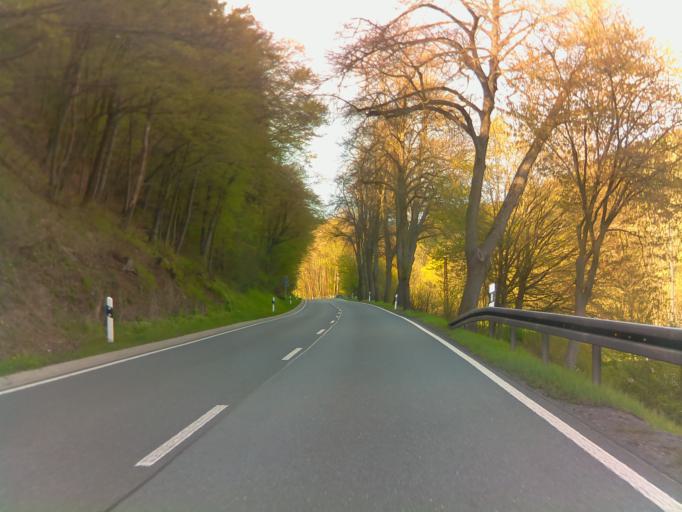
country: DE
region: Thuringia
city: Probstzella
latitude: 50.5728
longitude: 11.3695
